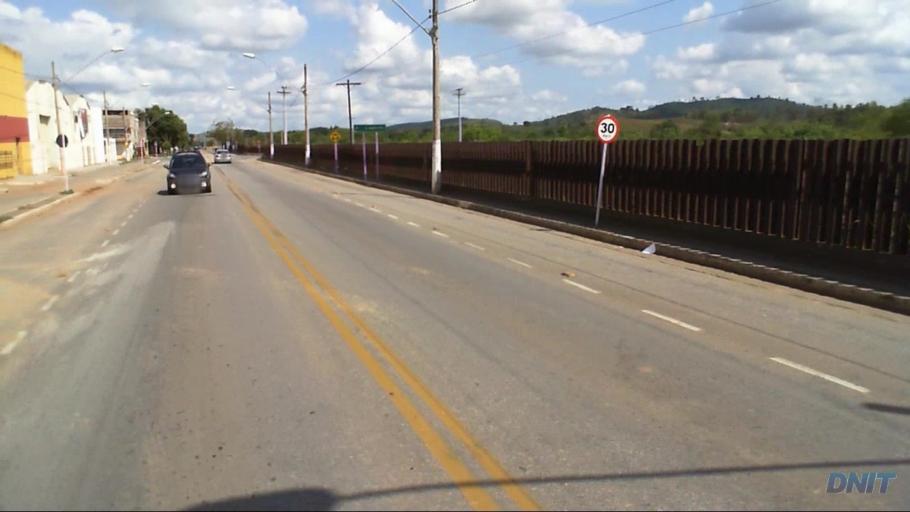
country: BR
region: Minas Gerais
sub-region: Governador Valadares
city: Governador Valadares
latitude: -18.9000
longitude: -41.9851
